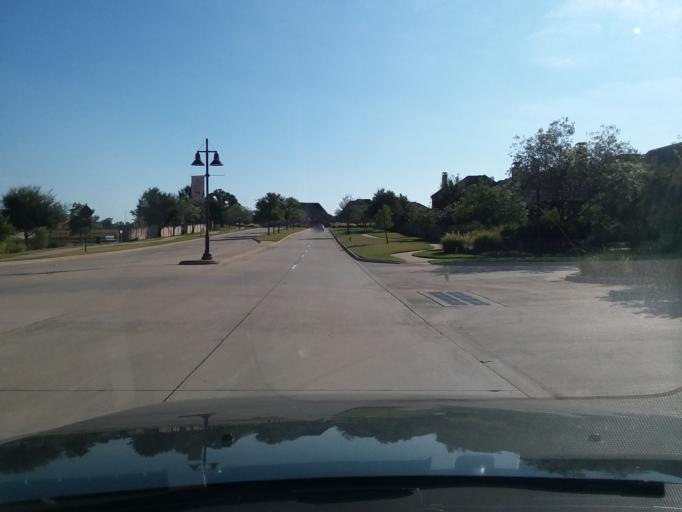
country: US
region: Texas
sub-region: Denton County
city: Copper Canyon
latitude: 33.1082
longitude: -97.1161
